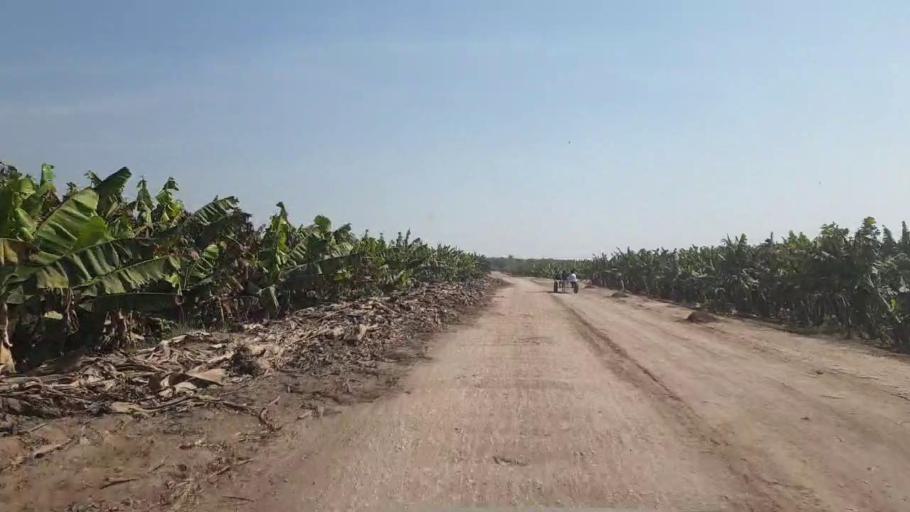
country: PK
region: Sindh
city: Chambar
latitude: 25.3632
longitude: 68.7883
